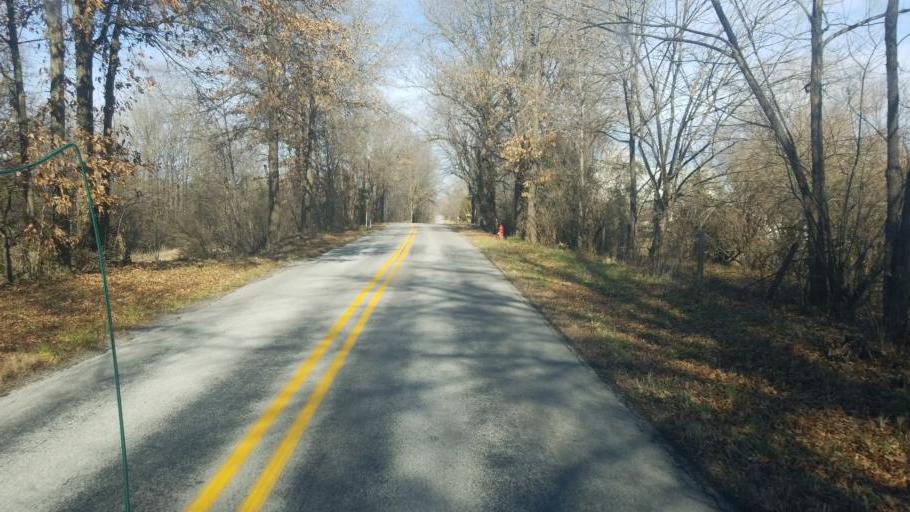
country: US
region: Illinois
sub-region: Jackson County
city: Carbondale
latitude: 37.6879
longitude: -89.2110
